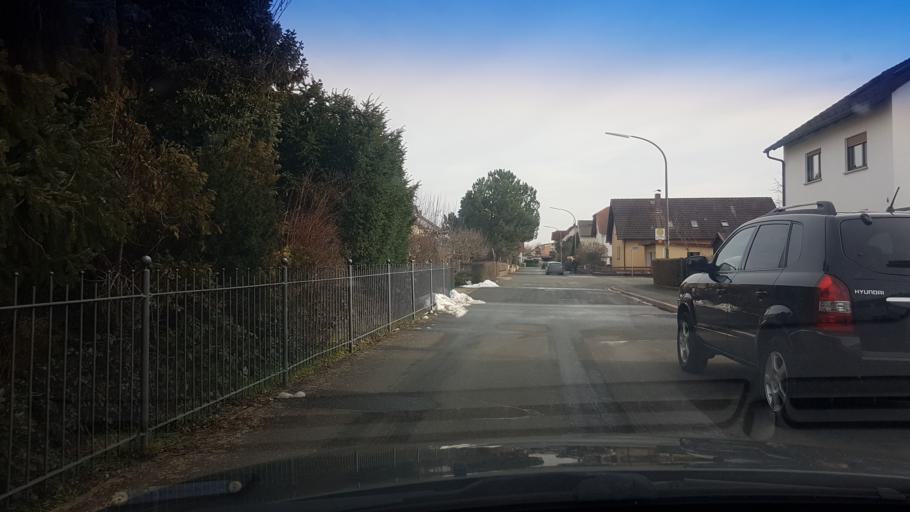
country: DE
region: Bavaria
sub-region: Upper Franconia
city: Hirschaid
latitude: 49.8237
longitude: 10.9917
